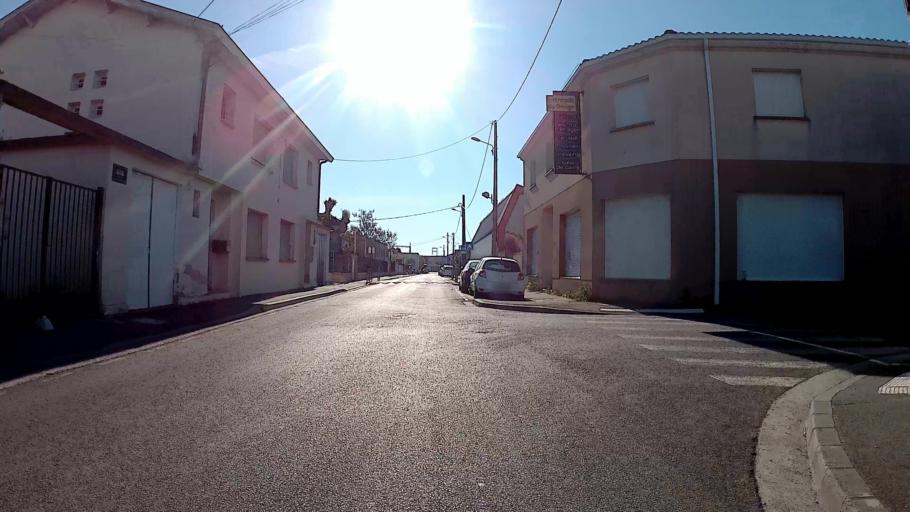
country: FR
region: Aquitaine
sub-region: Departement de la Gironde
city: Begles
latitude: 44.8164
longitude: -0.5450
